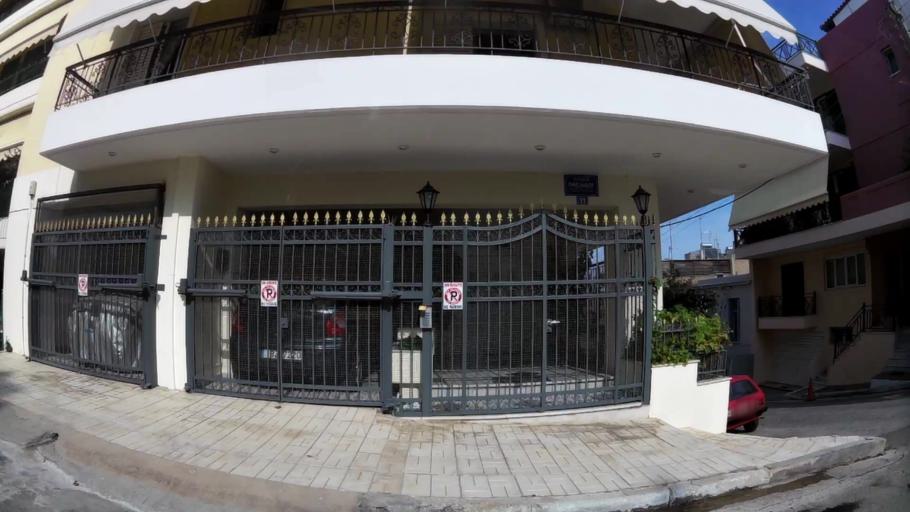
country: GR
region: Attica
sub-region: Nomarchia Athinas
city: Athens
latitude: 37.9660
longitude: 23.7128
